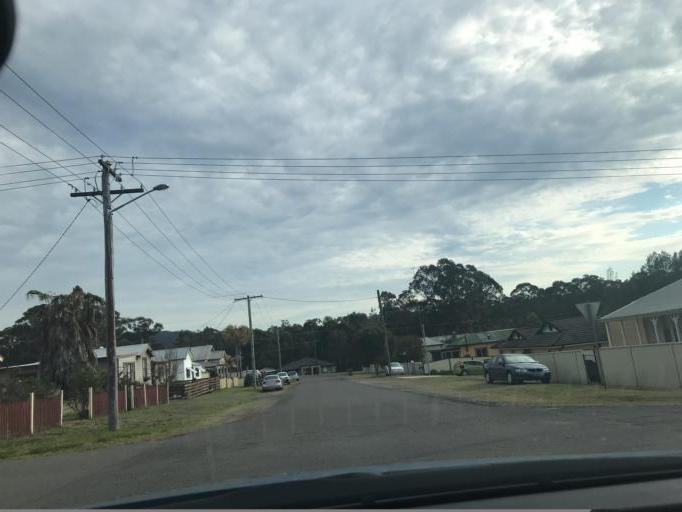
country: AU
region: New South Wales
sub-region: Cessnock
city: Cessnock
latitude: -32.9030
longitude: 151.2858
